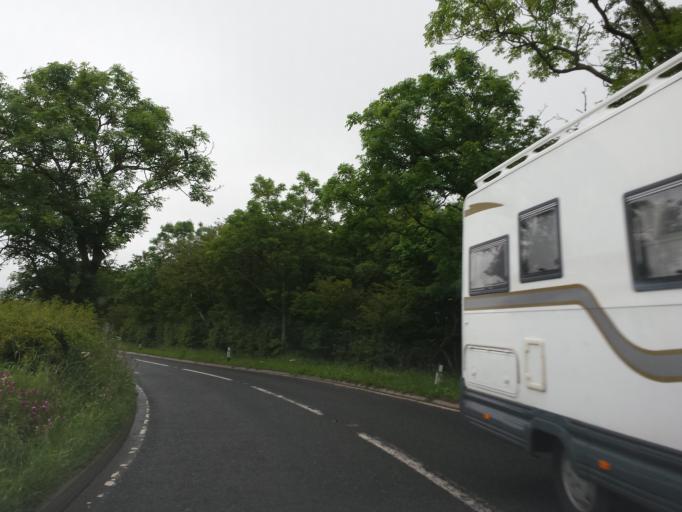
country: GB
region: Scotland
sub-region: Fife
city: Lundin Links
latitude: 56.2364
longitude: -2.8993
